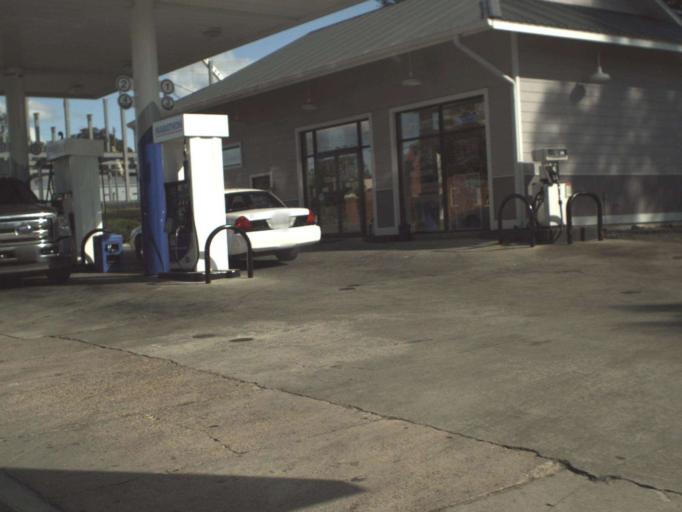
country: US
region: Florida
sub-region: Washington County
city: Chipley
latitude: 30.7791
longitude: -85.5426
